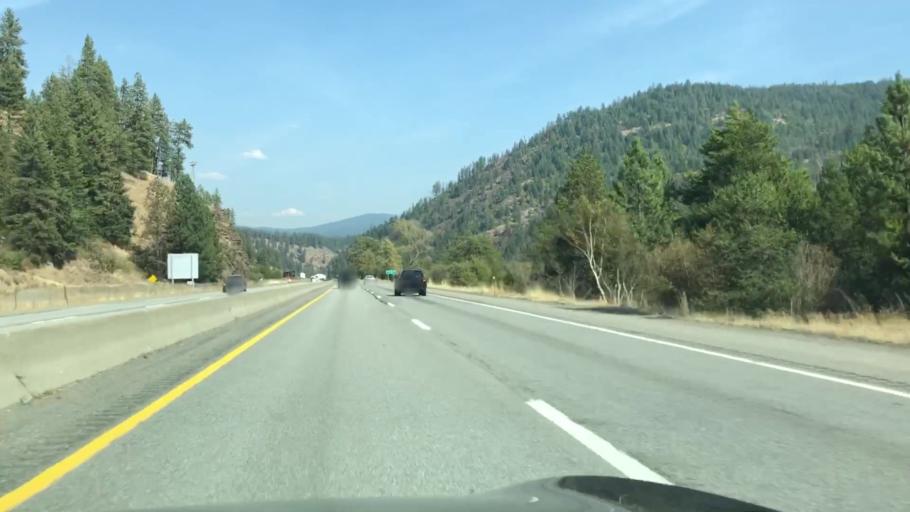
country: US
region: Idaho
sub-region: Kootenai County
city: Coeur d'Alene
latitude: 47.6262
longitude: -116.6350
